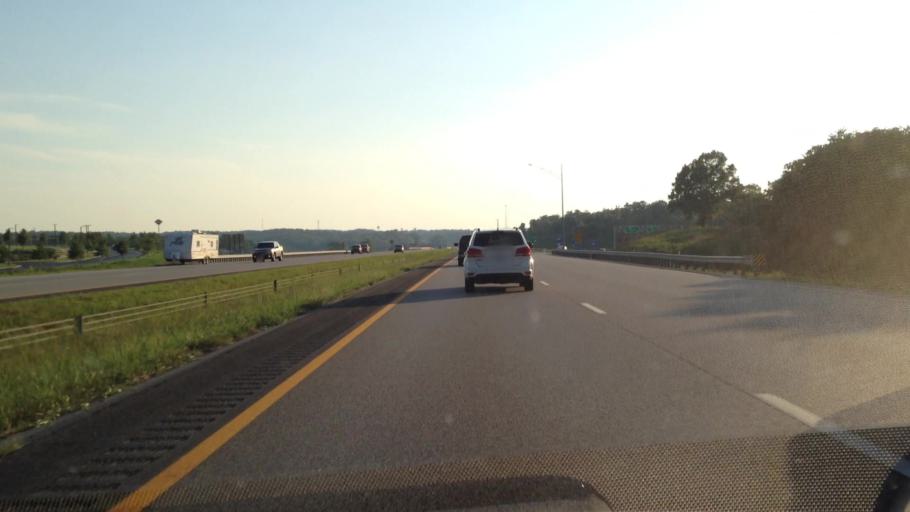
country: US
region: Missouri
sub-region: Jasper County
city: Joplin
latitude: 37.0392
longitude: -94.5106
